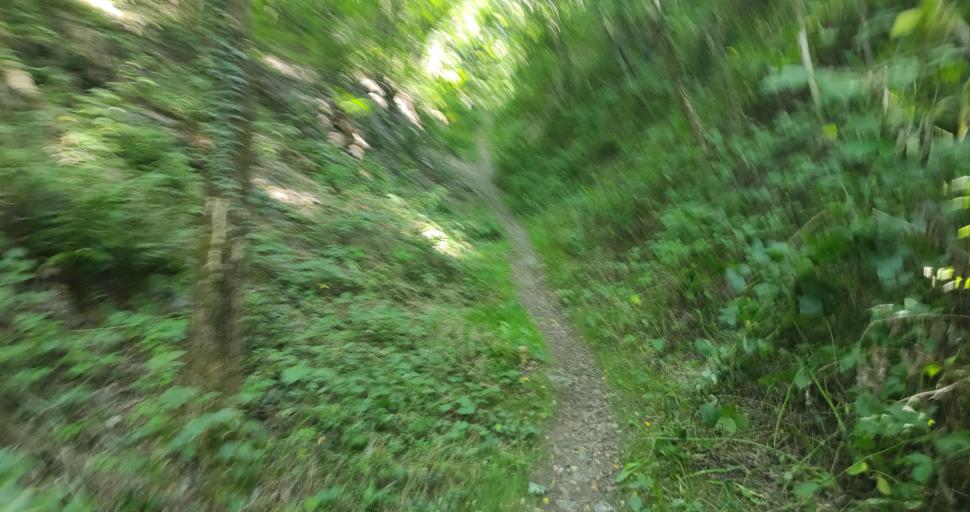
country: FR
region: Midi-Pyrenees
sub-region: Departement de l'Aveyron
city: Cransac
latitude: 44.5329
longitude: 2.2758
